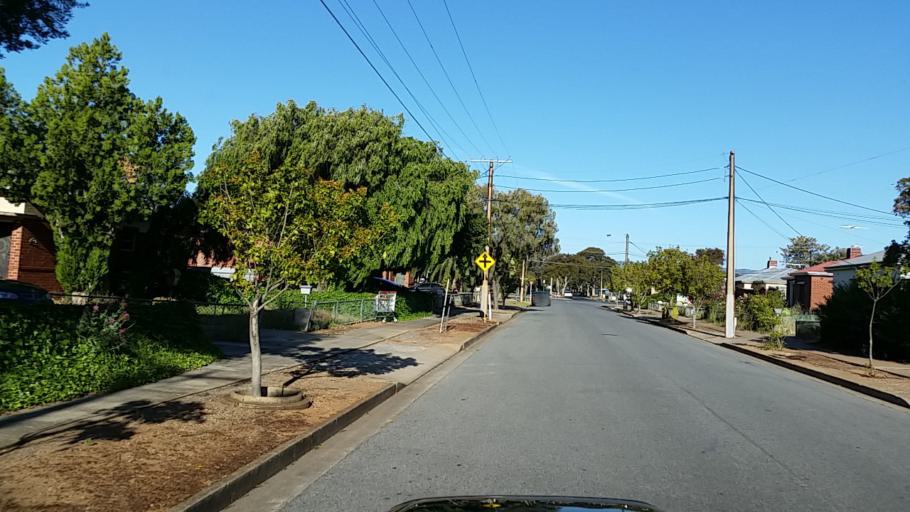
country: AU
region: South Australia
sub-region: Marion
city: South Plympton
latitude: -34.9783
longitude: 138.5635
